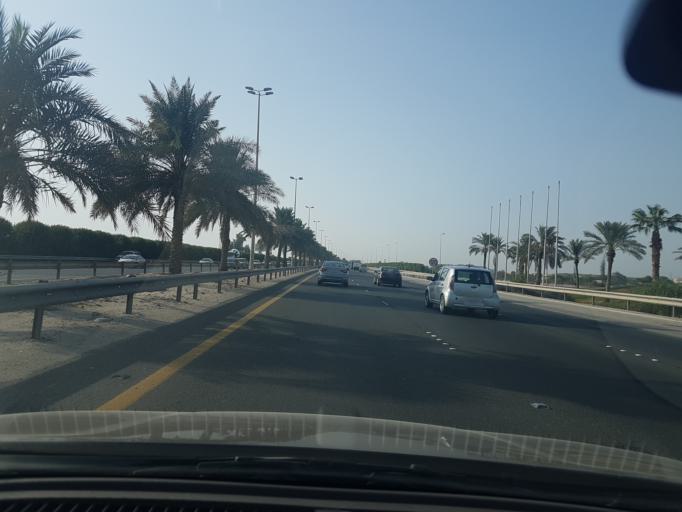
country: BH
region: Northern
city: Madinat `Isa
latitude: 26.1639
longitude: 50.5041
